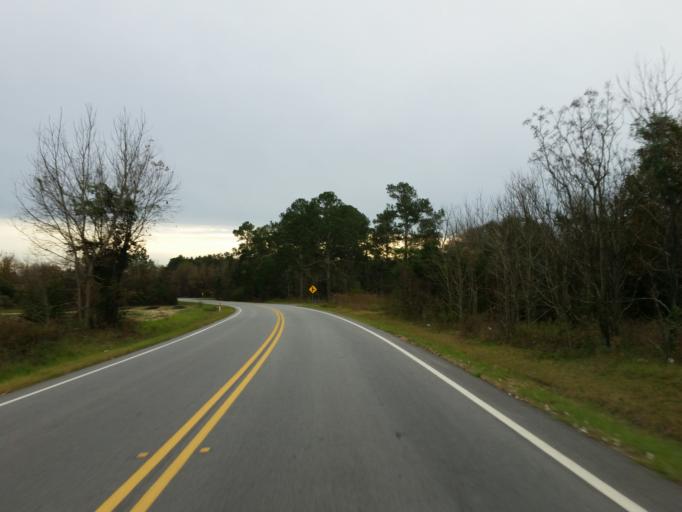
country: US
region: Georgia
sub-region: Crisp County
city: Cordele
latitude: 31.8404
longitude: -83.7446
